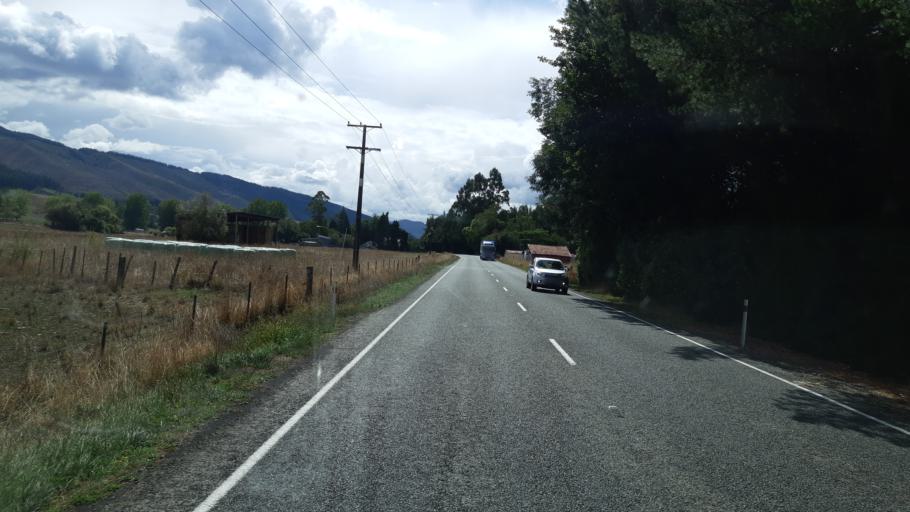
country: NZ
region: Tasman
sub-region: Tasman District
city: Wakefield
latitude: -41.4759
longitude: 172.8042
